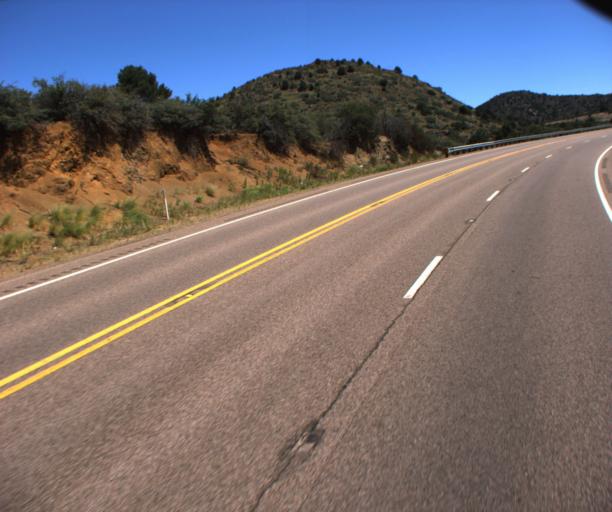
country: US
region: Arizona
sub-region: Gila County
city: Globe
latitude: 33.6380
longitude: -110.5828
